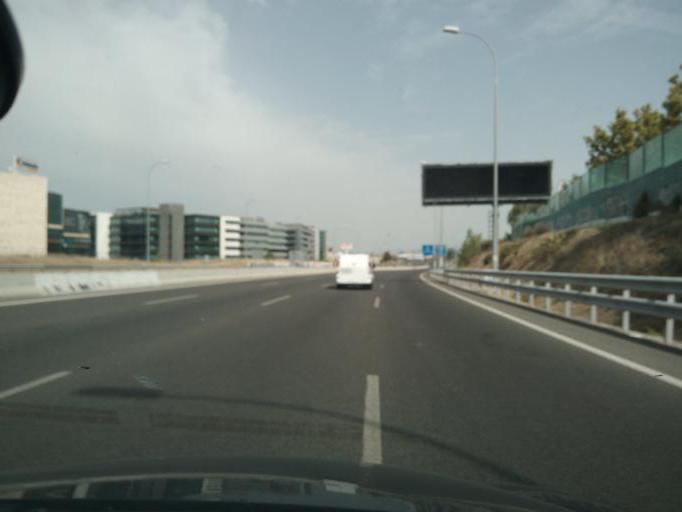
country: ES
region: Madrid
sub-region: Provincia de Madrid
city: Hortaleza
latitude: 40.4745
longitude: -3.6294
